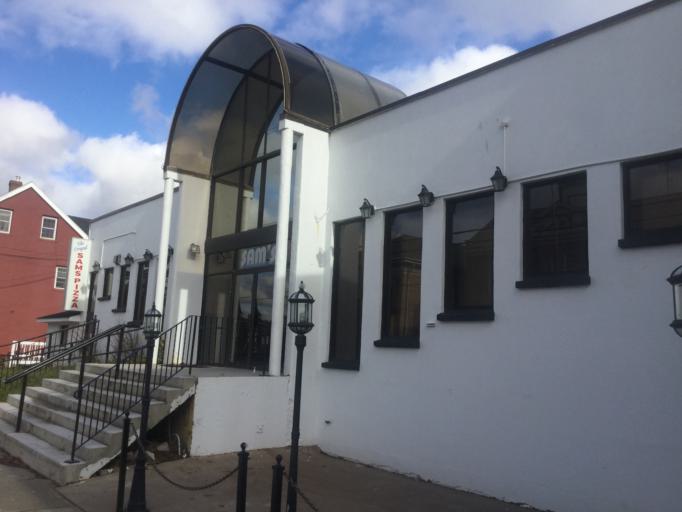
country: CA
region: Nova Scotia
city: New Glasgow
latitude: 45.5589
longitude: -62.6598
